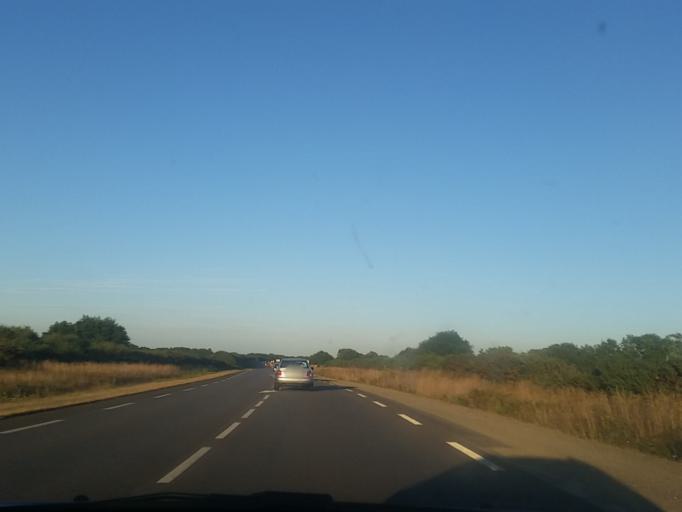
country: FR
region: Pays de la Loire
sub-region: Departement de la Loire-Atlantique
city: Rouans
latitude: 47.1878
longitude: -1.8183
